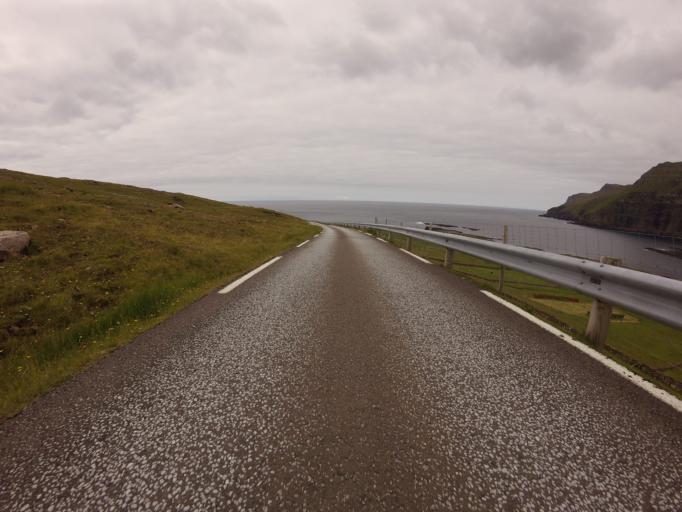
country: FO
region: Suduroy
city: Tvoroyri
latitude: 61.5189
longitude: -6.8833
